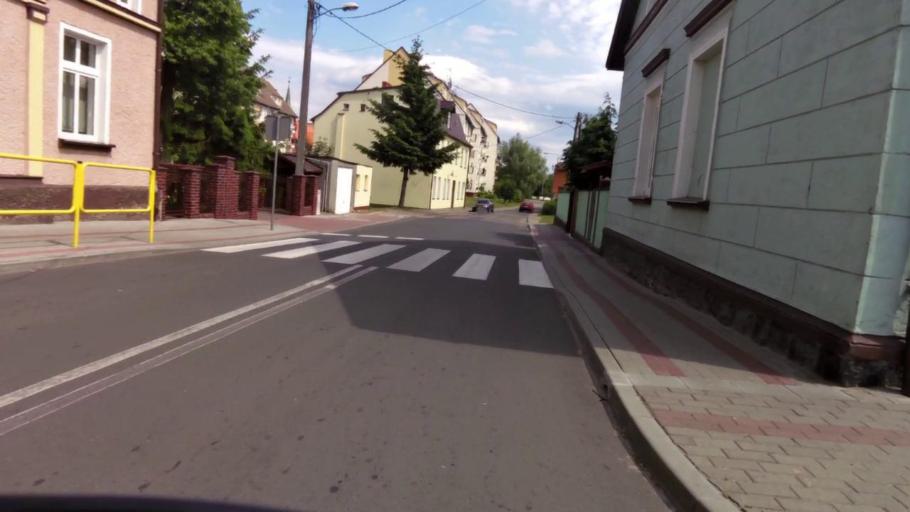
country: PL
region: West Pomeranian Voivodeship
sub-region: Powiat kamienski
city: Wolin
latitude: 53.8420
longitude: 14.6117
